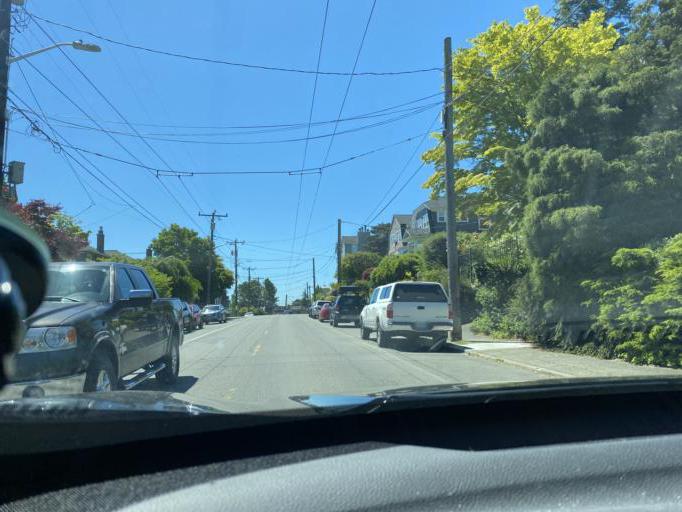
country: US
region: Washington
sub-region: King County
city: Seattle
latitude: 47.6374
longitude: -122.3471
